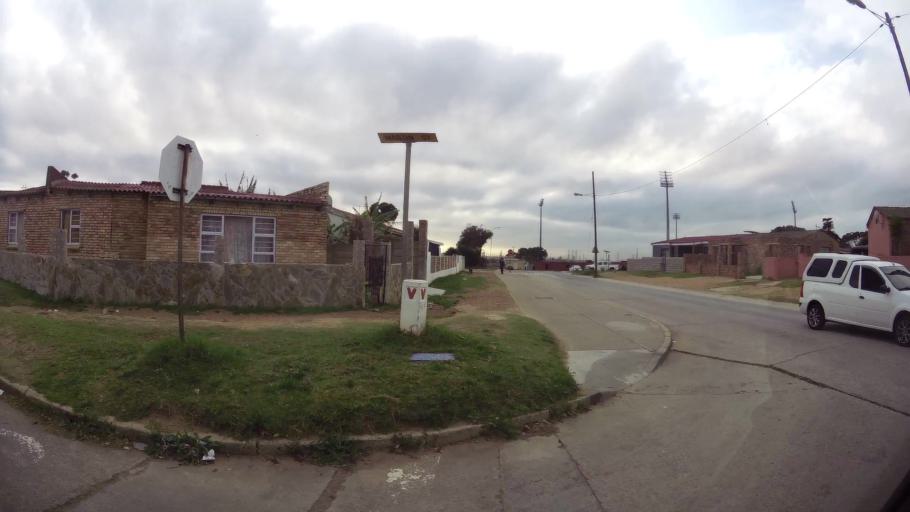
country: ZA
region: Eastern Cape
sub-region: Nelson Mandela Bay Metropolitan Municipality
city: Port Elizabeth
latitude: -33.9141
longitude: 25.5572
